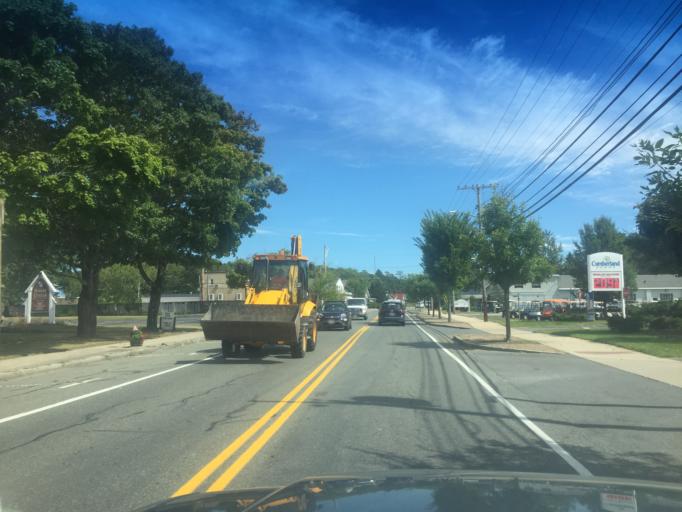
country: US
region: Massachusetts
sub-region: Barnstable County
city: Buzzards Bay
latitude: 41.7466
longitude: -70.6099
